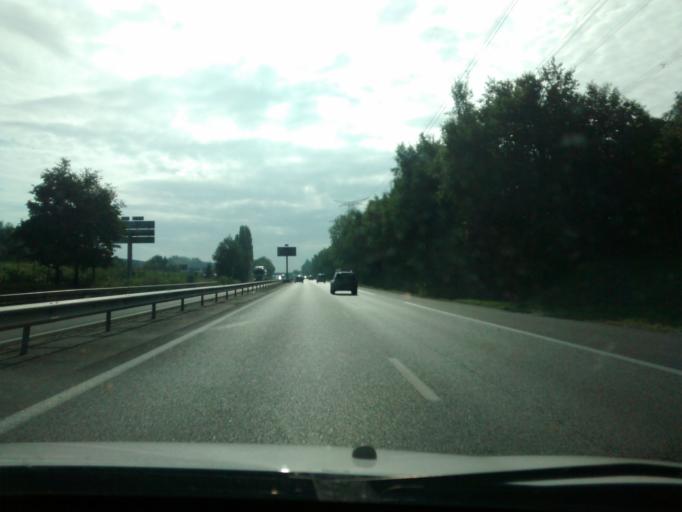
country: FR
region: Pays de la Loire
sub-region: Departement de la Mayenne
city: Saint-Pierre-la-Cour
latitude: 48.0852
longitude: -1.0544
